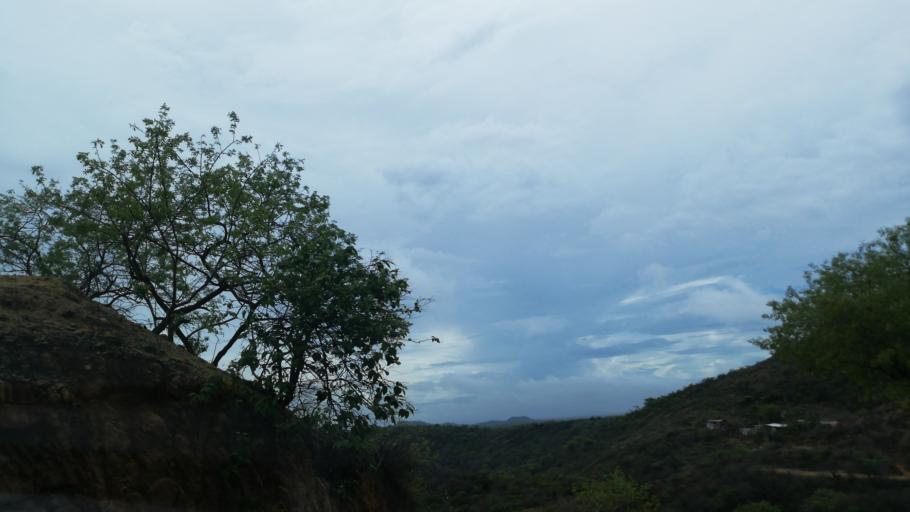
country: MX
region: Oaxaca
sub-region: Salina Cruz
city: Salina Cruz
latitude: 16.1811
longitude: -95.1802
